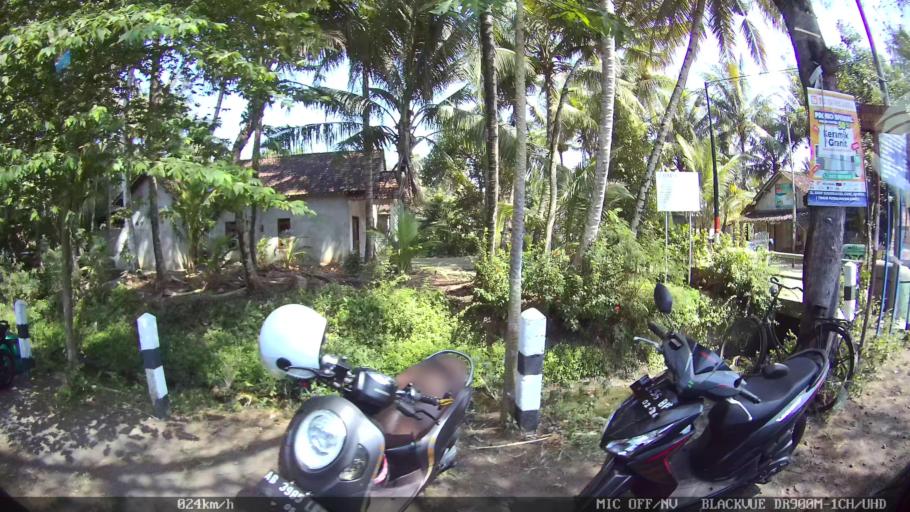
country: ID
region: Daerah Istimewa Yogyakarta
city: Srandakan
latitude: -7.9238
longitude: 110.1572
